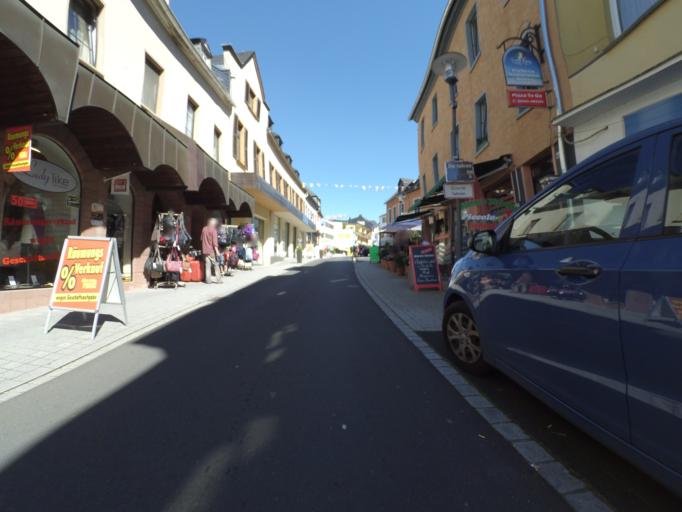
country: DE
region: Rheinland-Pfalz
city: Gerolstein
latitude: 50.2221
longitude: 6.6620
